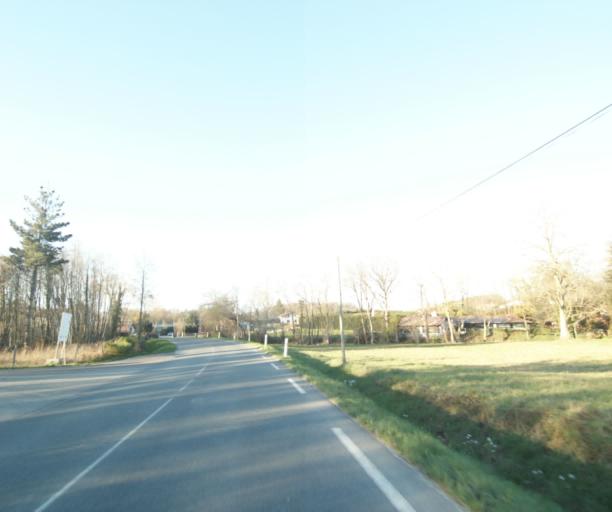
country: FR
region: Aquitaine
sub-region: Departement des Pyrenees-Atlantiques
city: Urrugne
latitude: 43.3595
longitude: -1.6921
